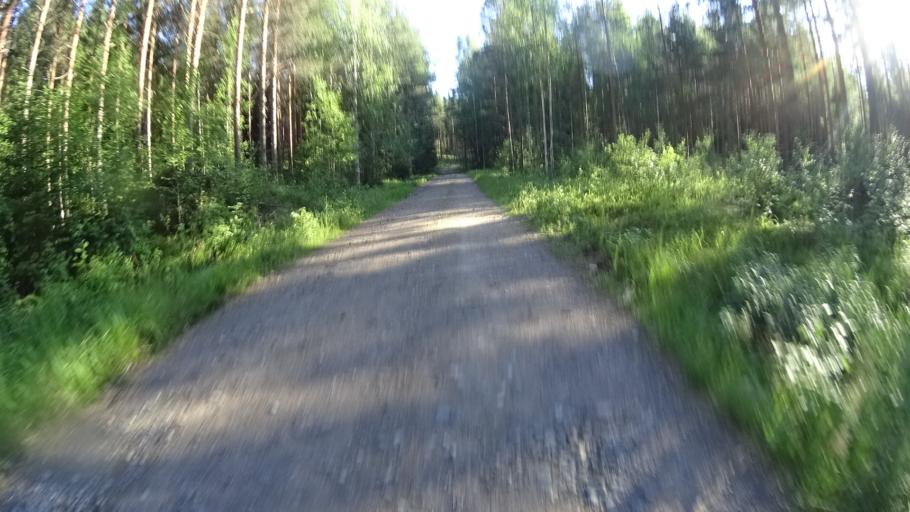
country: FI
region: Uusimaa
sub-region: Helsinki
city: Karkkila
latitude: 60.6516
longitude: 24.1287
